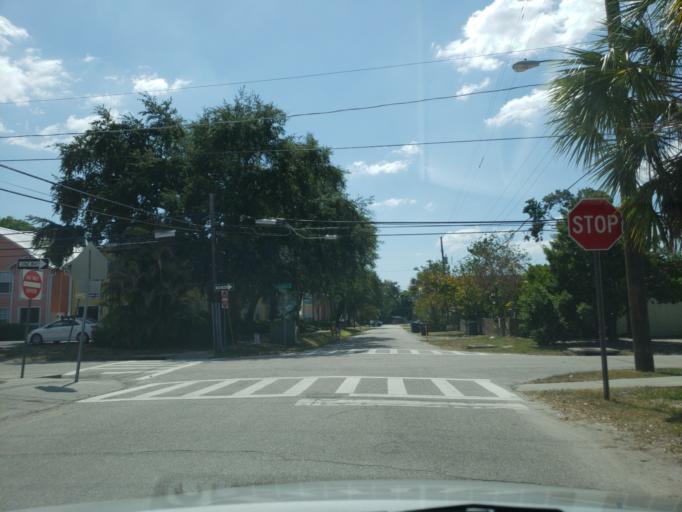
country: US
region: Florida
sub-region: Hillsborough County
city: Tampa
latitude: 27.9436
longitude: -82.4911
